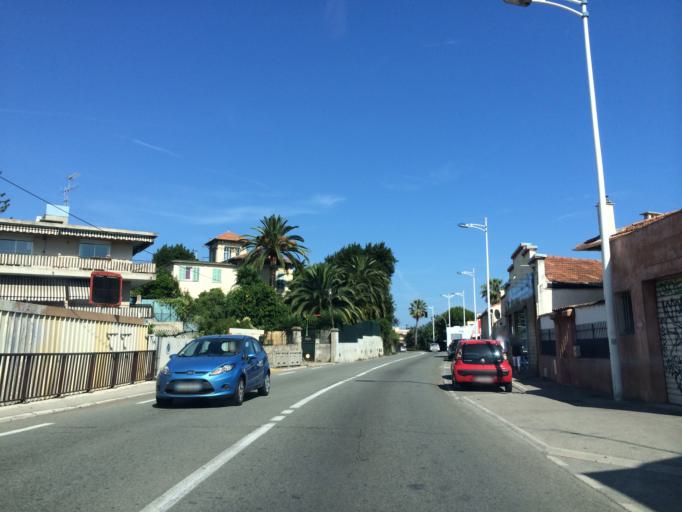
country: FR
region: Provence-Alpes-Cote d'Azur
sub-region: Departement des Alpes-Maritimes
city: Saint-Laurent-du-Var
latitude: 43.6607
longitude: 7.1783
